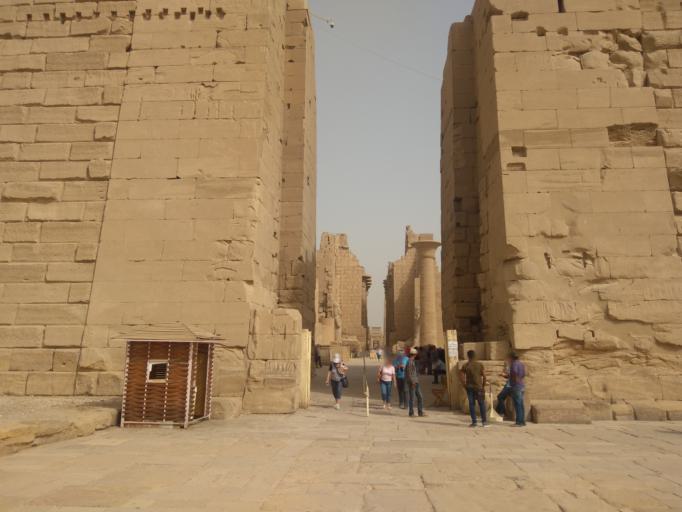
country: EG
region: Luxor
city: Luxor
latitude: 25.7193
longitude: 32.6564
